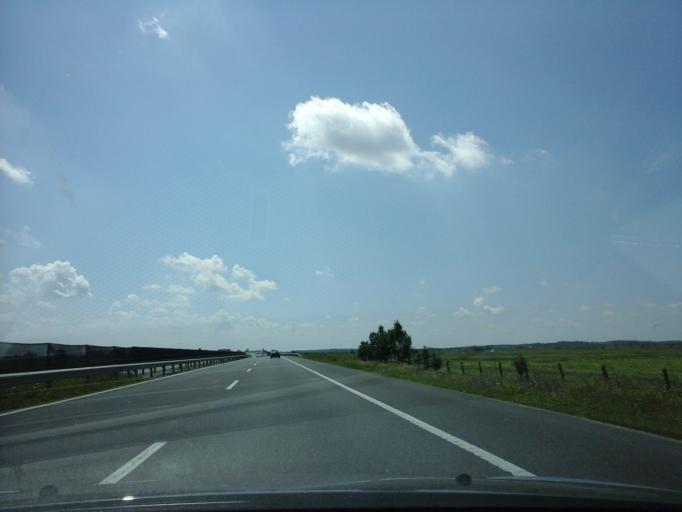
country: HU
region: Hajdu-Bihar
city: Polgar
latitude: 47.8321
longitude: 21.1513
